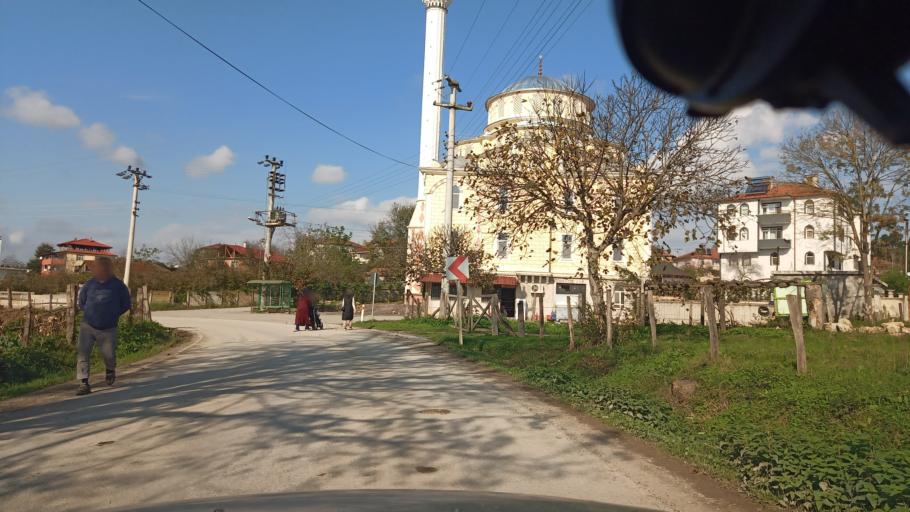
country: TR
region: Sakarya
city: Kaynarca
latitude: 41.0996
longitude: 30.4349
